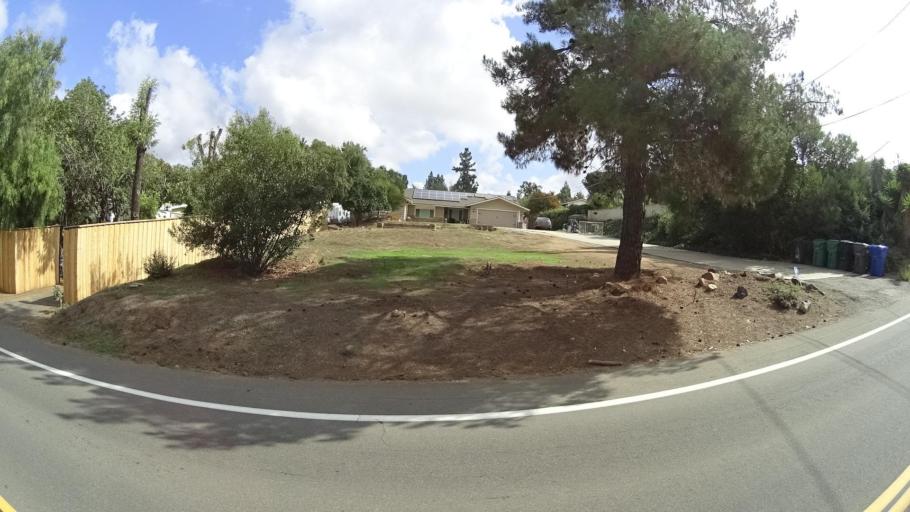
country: US
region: California
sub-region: San Diego County
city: Granite Hills
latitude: 32.7789
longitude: -116.9062
